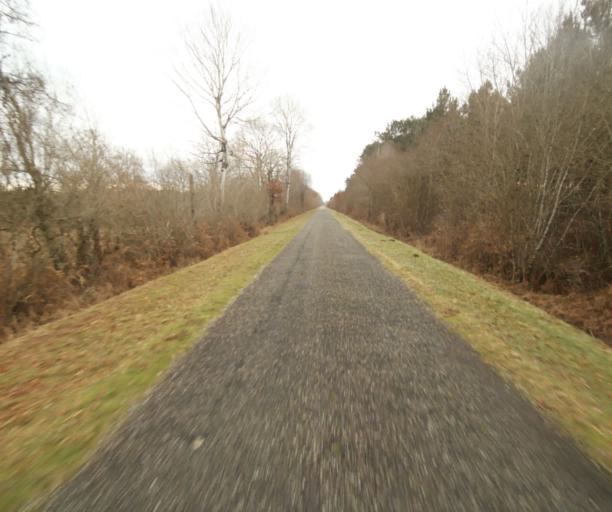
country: FR
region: Aquitaine
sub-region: Departement des Landes
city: Gabarret
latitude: 44.0223
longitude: -0.0472
